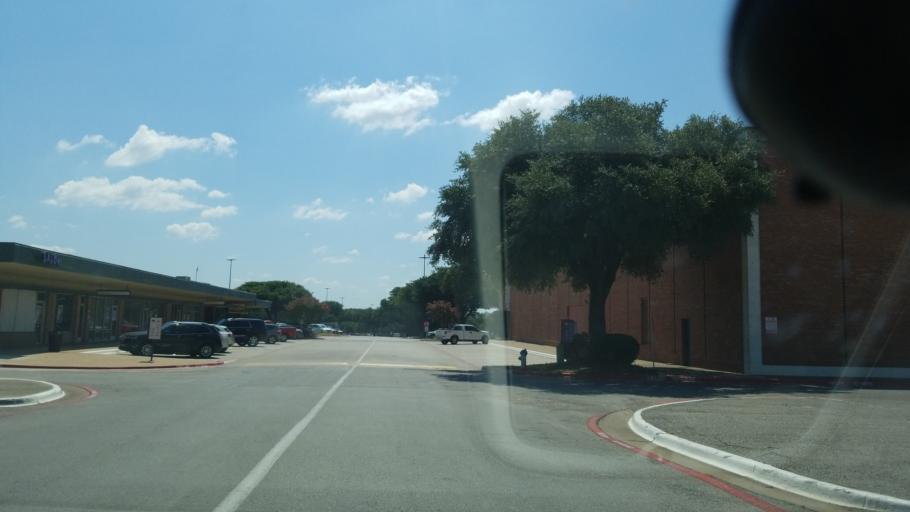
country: US
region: Texas
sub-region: Dallas County
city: Cockrell Hill
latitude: 32.7250
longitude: -96.8353
